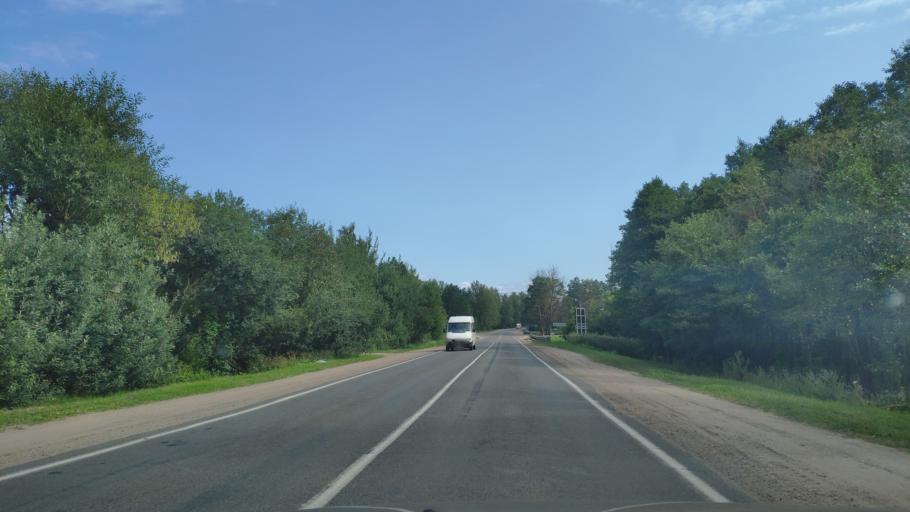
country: BY
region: Minsk
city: Zaslawye
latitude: 53.9843
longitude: 27.2558
